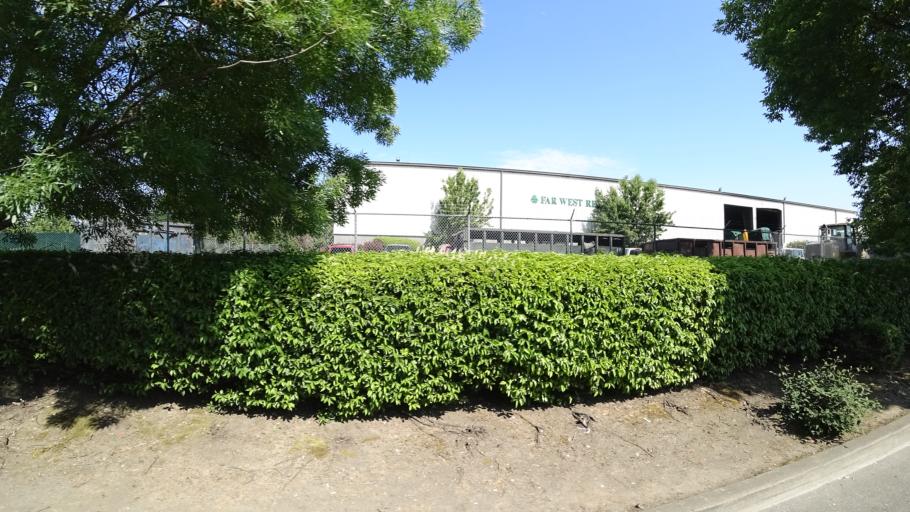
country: US
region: Oregon
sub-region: Multnomah County
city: Lents
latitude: 45.5583
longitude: -122.5320
